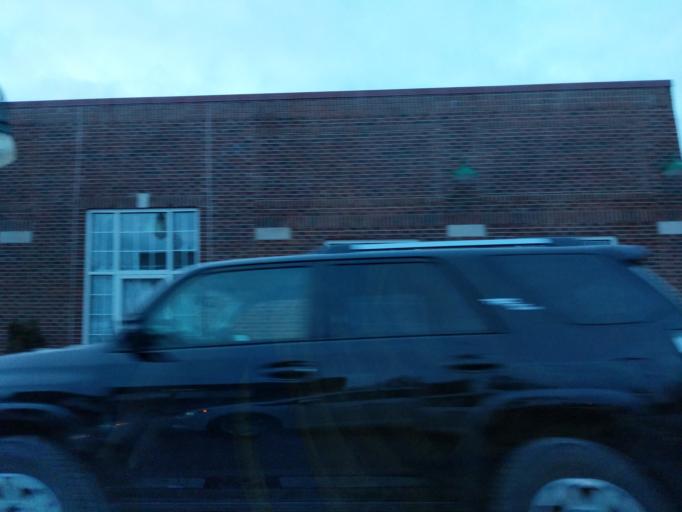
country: US
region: Michigan
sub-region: Lapeer County
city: Almont
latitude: 42.9192
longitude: -83.0451
